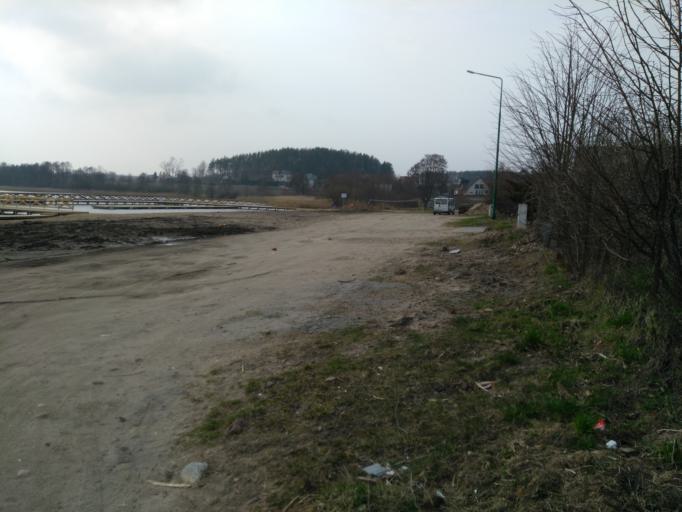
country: PL
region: Pomeranian Voivodeship
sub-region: Powiat kartuski
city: Suleczyno
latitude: 54.3228
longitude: 17.7933
